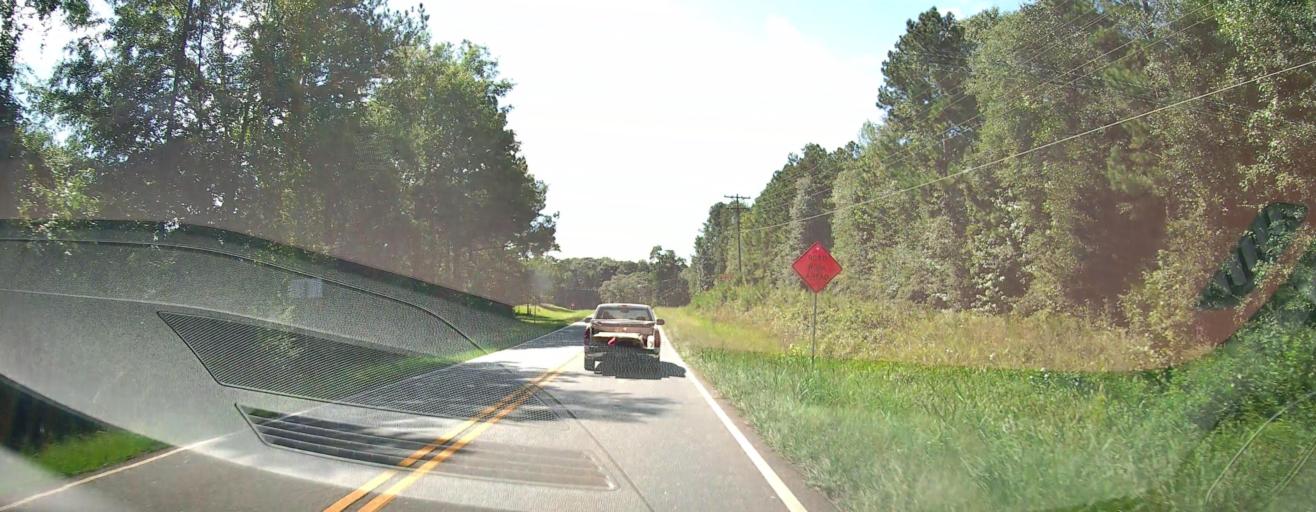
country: US
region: Georgia
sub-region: Upson County
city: Hannahs Mill
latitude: 32.9516
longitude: -84.3005
